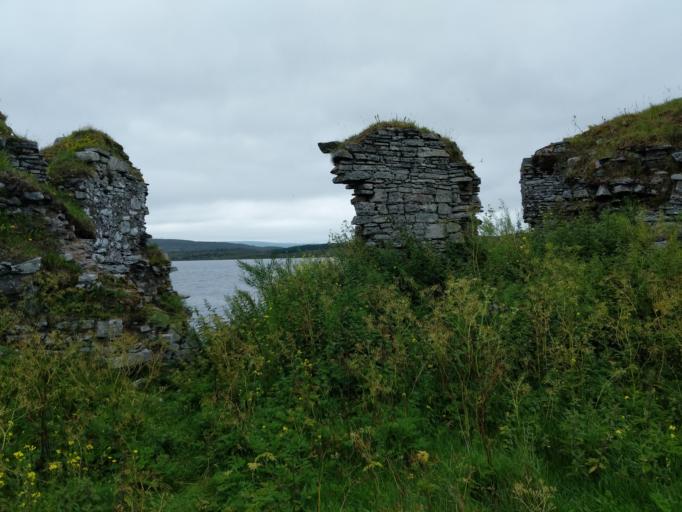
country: GB
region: Scotland
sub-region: Highland
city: Grantown on Spey
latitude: 57.4056
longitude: -3.7085
